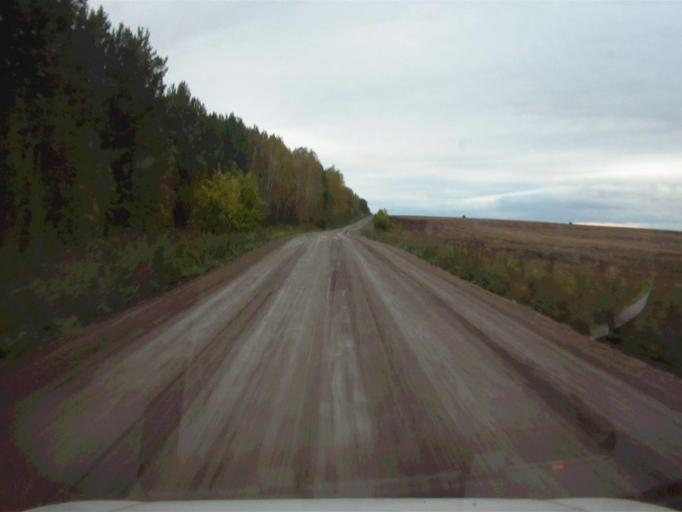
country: RU
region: Sverdlovsk
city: Mikhaylovsk
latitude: 56.1502
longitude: 59.2705
